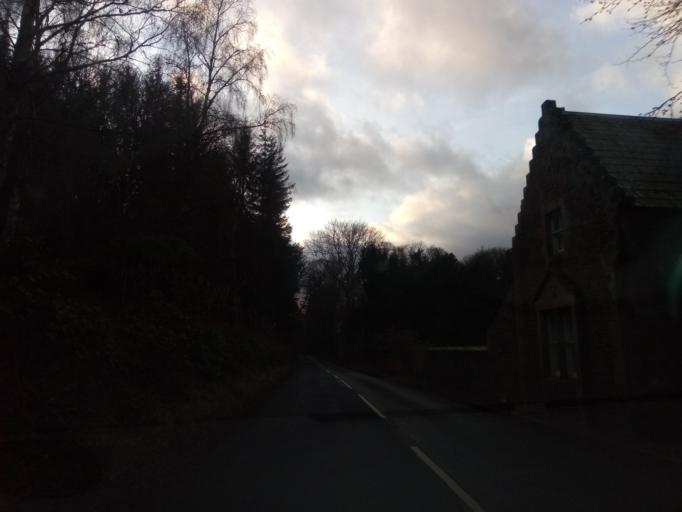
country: GB
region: Scotland
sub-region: The Scottish Borders
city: Galashiels
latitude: 55.5979
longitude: -2.7831
